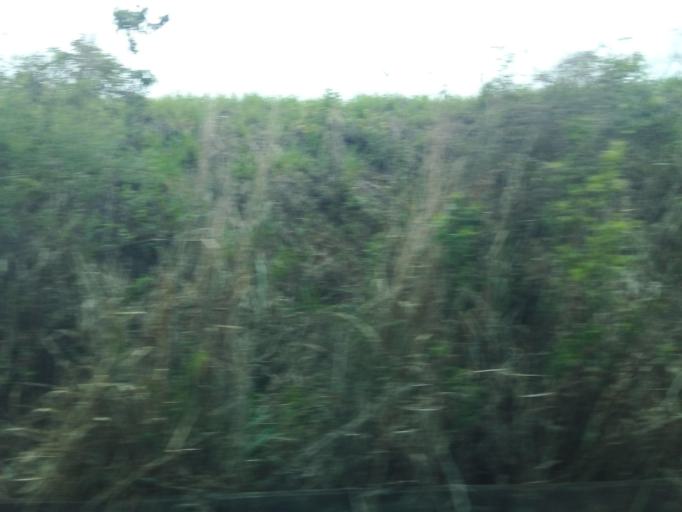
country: BR
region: Minas Gerais
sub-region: Ipatinga
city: Ipatinga
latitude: -19.4643
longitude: -42.4741
